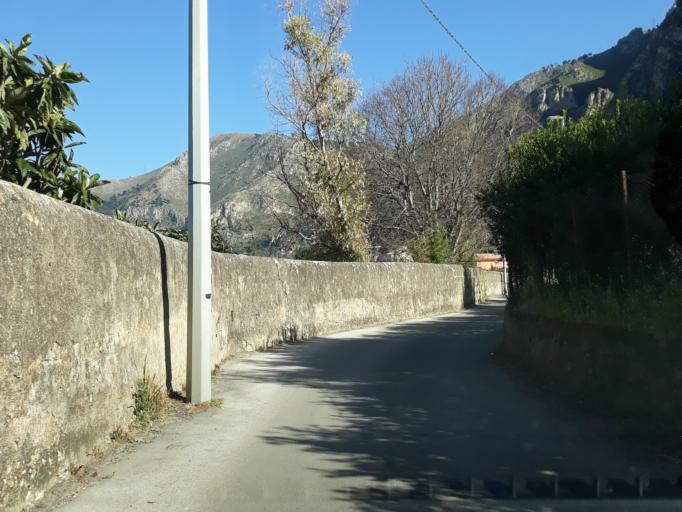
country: IT
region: Sicily
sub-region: Palermo
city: Villa Ciambra
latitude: 38.0764
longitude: 13.3487
